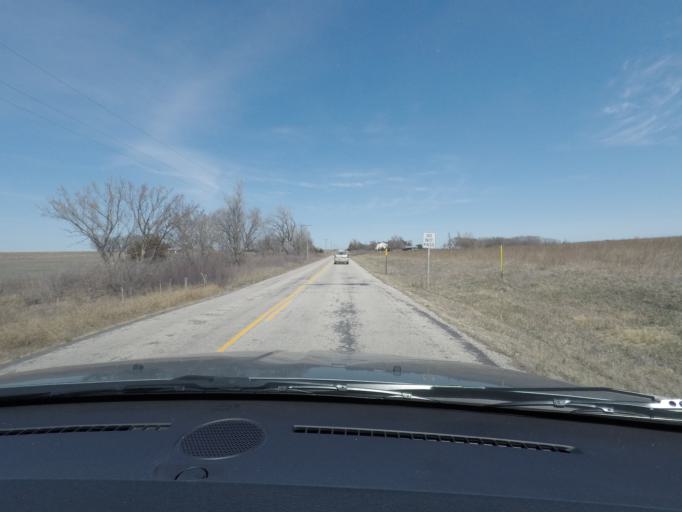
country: US
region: Kansas
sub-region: Lyon County
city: Emporia
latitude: 38.6257
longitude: -96.1696
